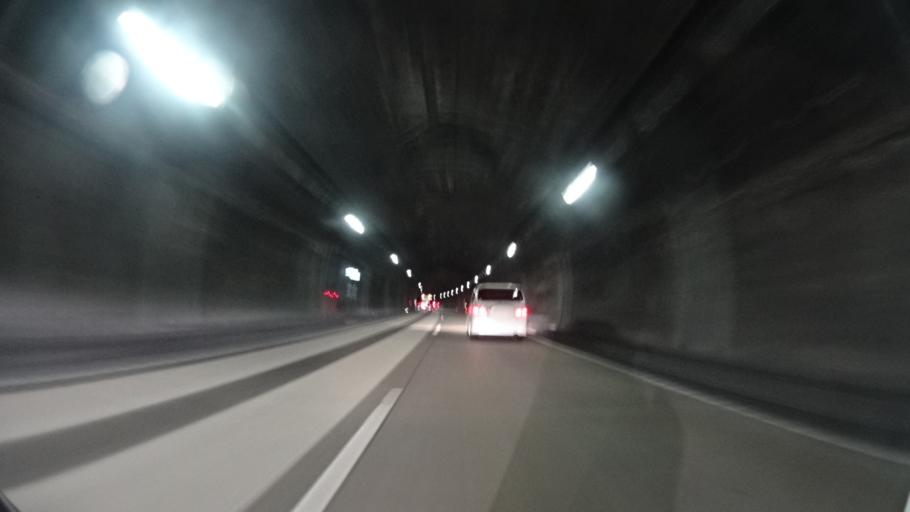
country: JP
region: Hyogo
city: Himeji
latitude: 34.8546
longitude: 134.7296
